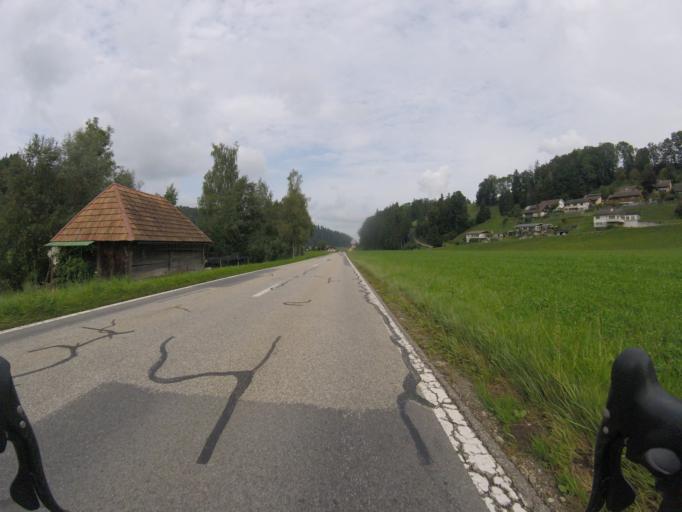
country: CH
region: Bern
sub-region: Emmental District
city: Lutzelfluh
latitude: 46.9909
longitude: 7.6897
